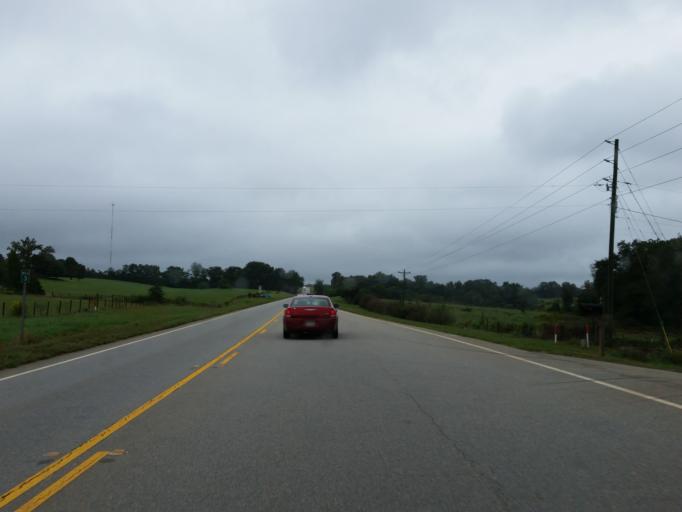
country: US
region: Georgia
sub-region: Lamar County
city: Barnesville
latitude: 32.8888
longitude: -84.0861
